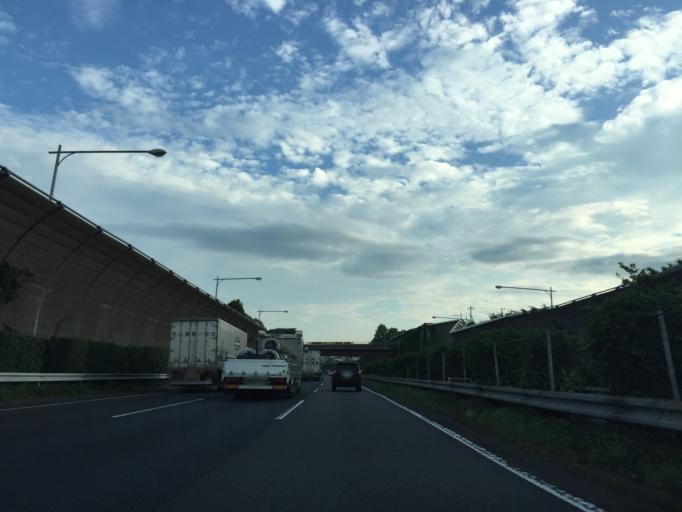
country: JP
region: Kanagawa
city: Isehara
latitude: 35.3782
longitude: 139.2680
